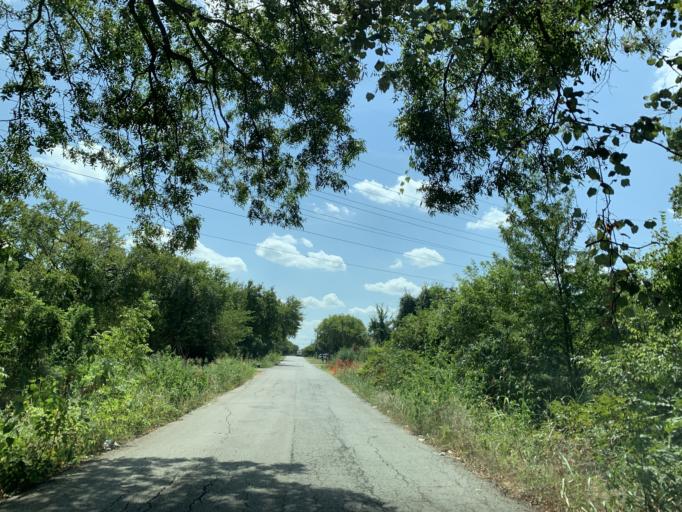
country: US
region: Texas
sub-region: Dallas County
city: Dallas
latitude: 32.7121
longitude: -96.7771
